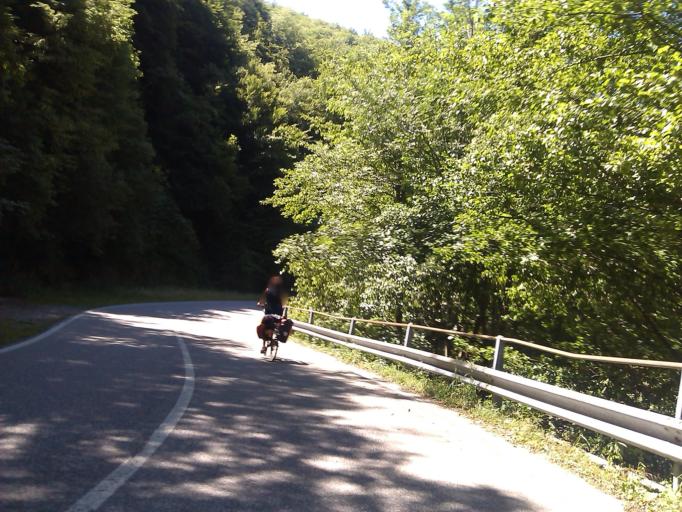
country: IT
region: Tuscany
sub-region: Provincia di Prato
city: Cantagallo
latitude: 44.0494
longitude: 11.0439
